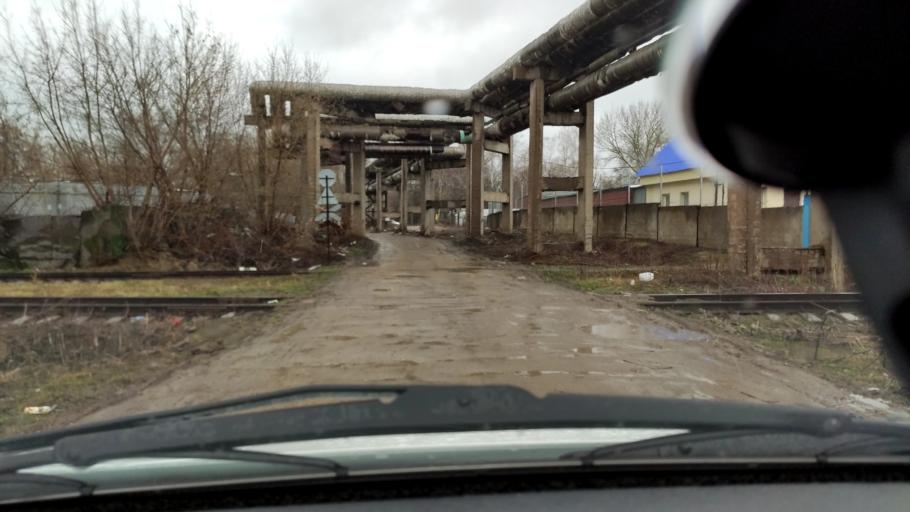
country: RU
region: Bashkortostan
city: Ufa
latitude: 54.7981
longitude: 56.1010
